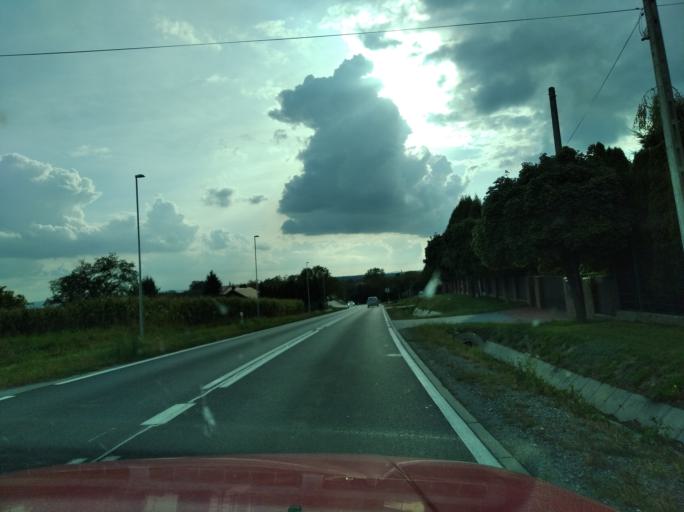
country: PL
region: Subcarpathian Voivodeship
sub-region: Powiat jaroslawski
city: Pawlosiow
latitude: 49.9861
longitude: 22.6557
